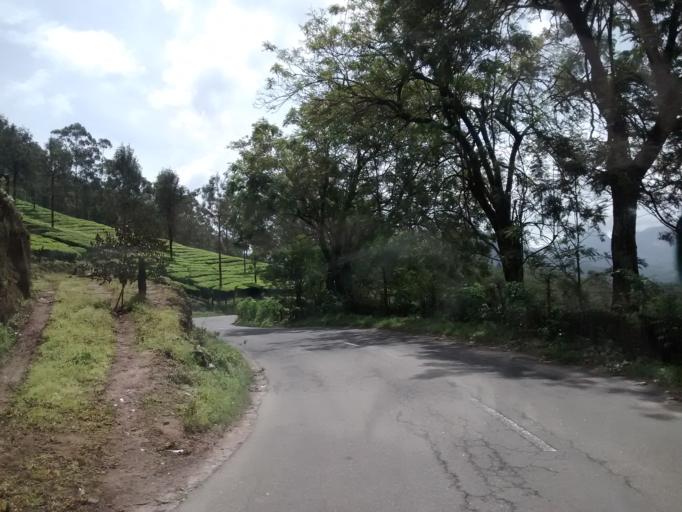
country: IN
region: Kerala
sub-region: Idukki
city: Munnar
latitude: 10.0935
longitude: 77.0935
